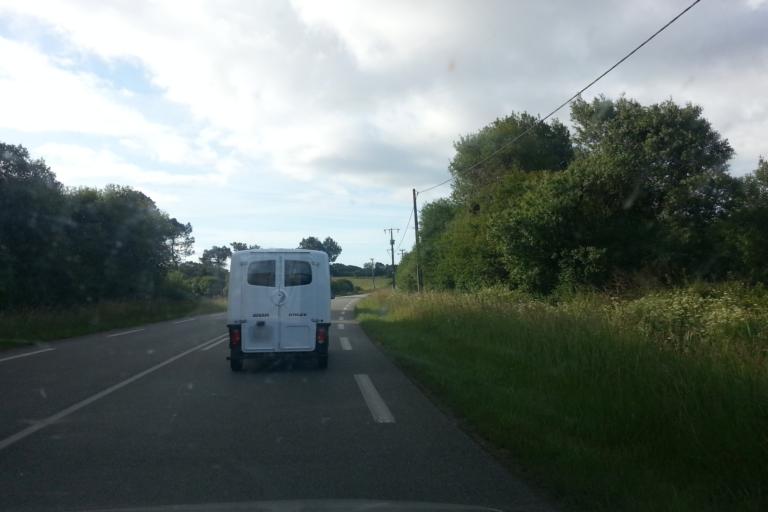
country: FR
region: Brittany
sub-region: Departement du Morbihan
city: Merlevenez
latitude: 47.7166
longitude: -3.2262
